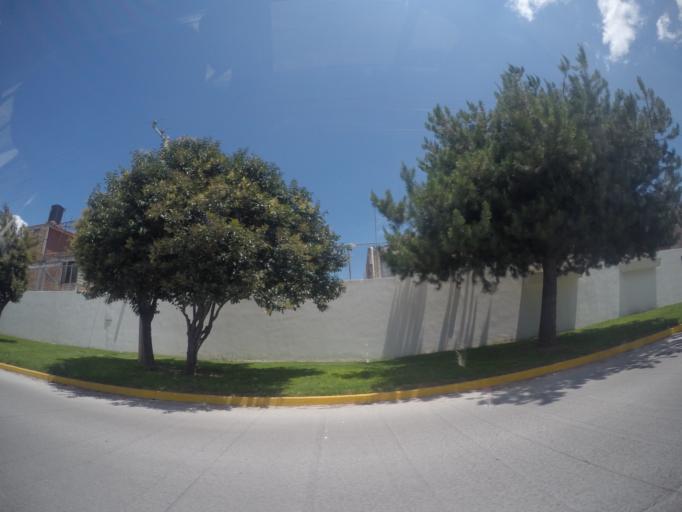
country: MX
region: Hidalgo
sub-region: Mineral de la Reforma
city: Campestre Villas del Alamo
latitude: 20.0964
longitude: -98.7125
